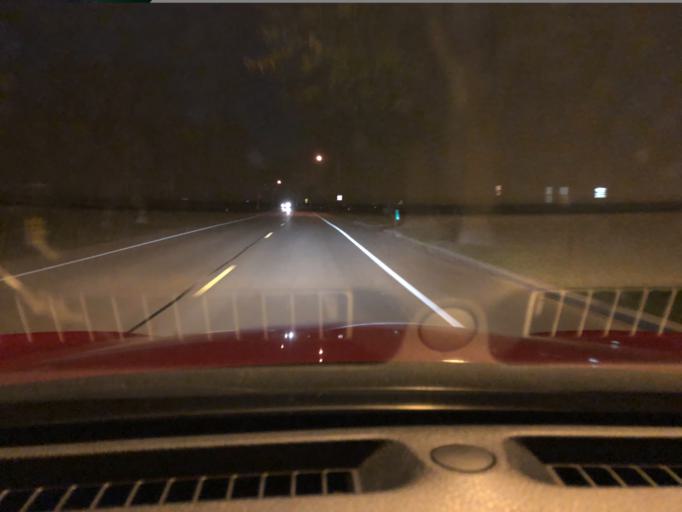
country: US
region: Indiana
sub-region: Steuben County
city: Hamilton
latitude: 41.5313
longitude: -84.9064
